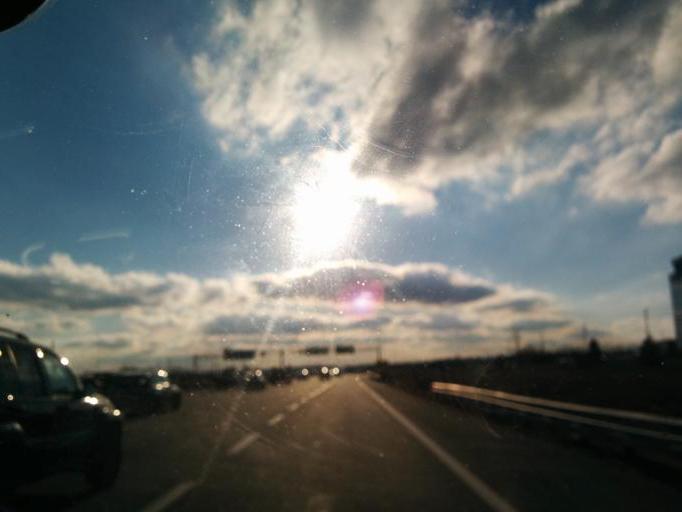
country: CA
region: Ontario
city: Oakville
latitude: 43.5045
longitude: -79.6697
